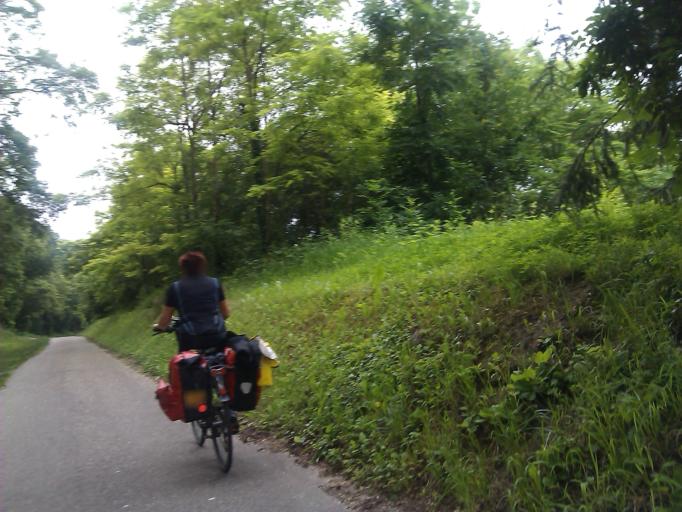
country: DE
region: Baden-Wuerttemberg
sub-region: Regierungsbezirk Stuttgart
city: Lowenstein
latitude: 49.0927
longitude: 9.3841
